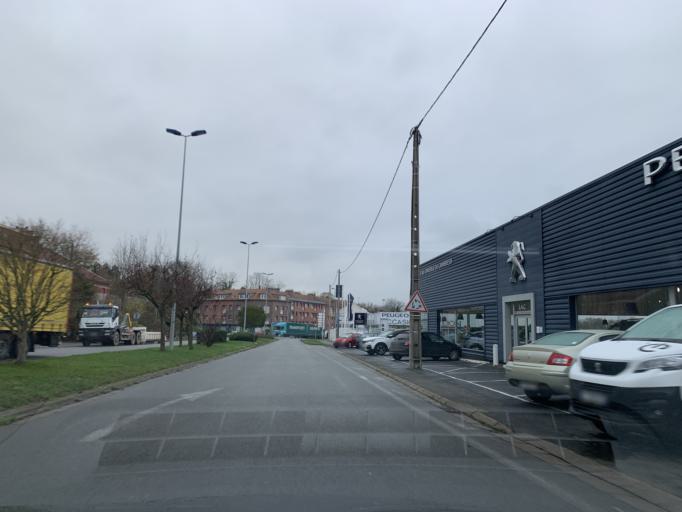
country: FR
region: Nord-Pas-de-Calais
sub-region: Departement du Nord
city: Neuville-Saint-Remy
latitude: 50.1822
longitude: 3.2362
